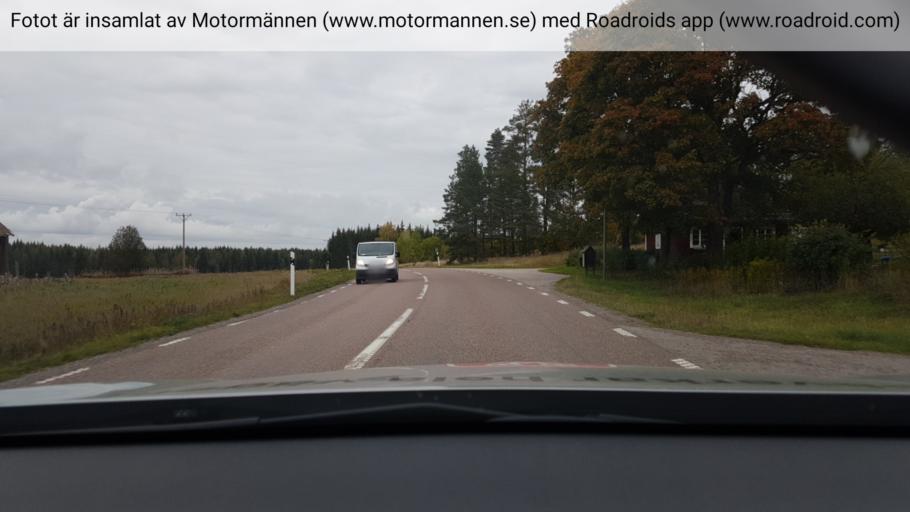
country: SE
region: Gaevleborg
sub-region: Gavle Kommun
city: Hedesunda
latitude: 60.4859
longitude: 16.9364
